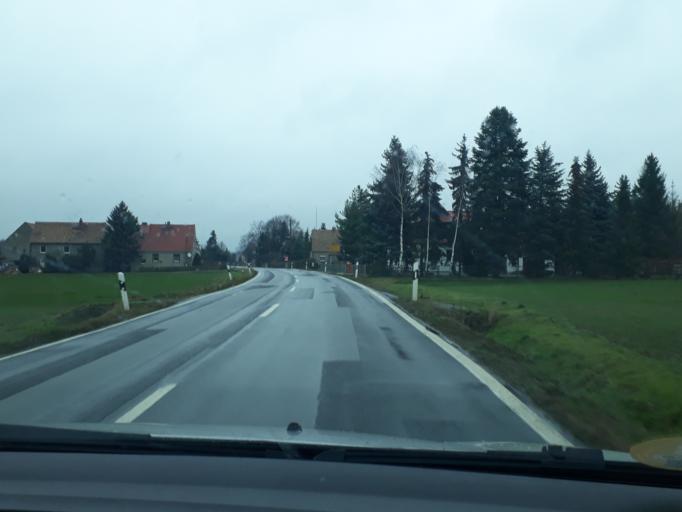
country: DE
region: Saxony
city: Malschwitz
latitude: 51.2230
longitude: 14.5031
